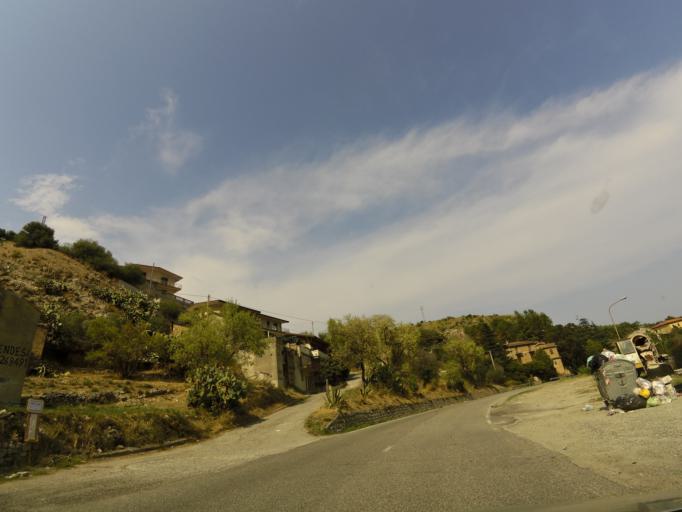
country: IT
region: Calabria
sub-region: Provincia di Reggio Calabria
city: Stilo
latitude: 38.4668
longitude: 16.5027
